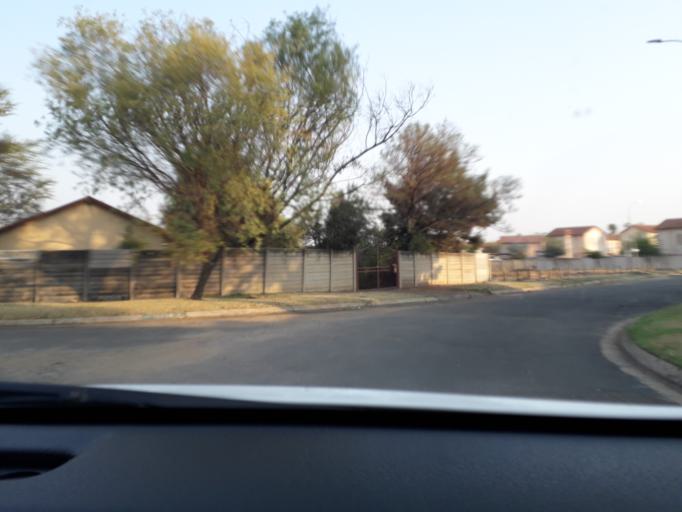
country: ZA
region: Gauteng
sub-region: City of Johannesburg Metropolitan Municipality
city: Modderfontein
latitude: -26.0658
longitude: 28.1990
